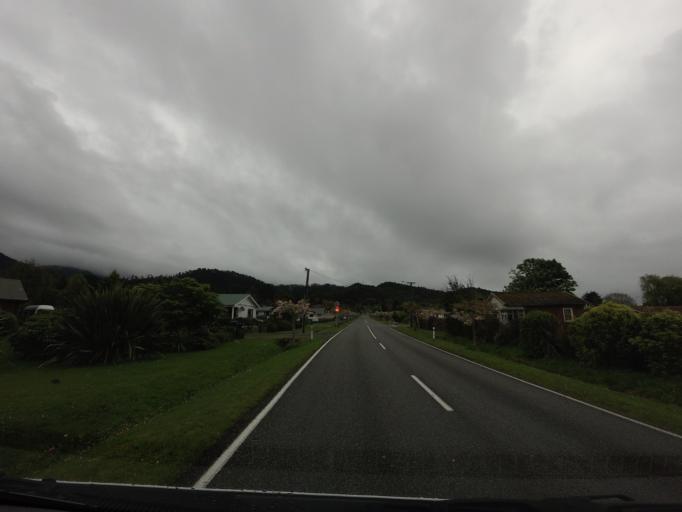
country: NZ
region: West Coast
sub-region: Westland District
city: Hokitika
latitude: -42.8978
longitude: 170.8204
